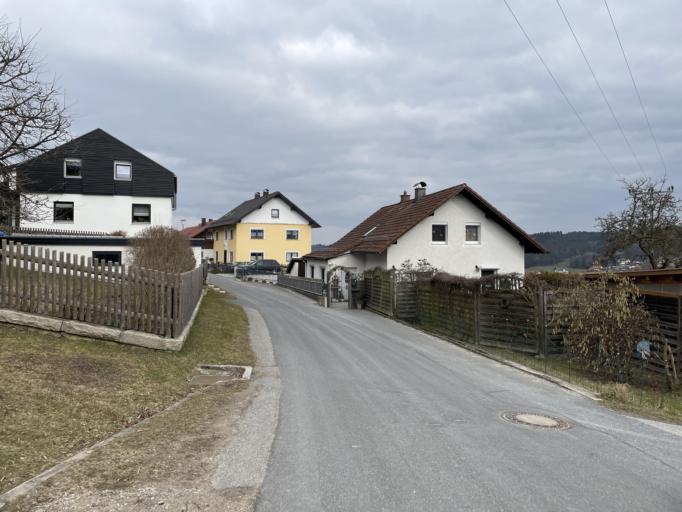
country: DE
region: Bavaria
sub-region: Upper Palatinate
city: Runding
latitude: 49.2174
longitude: 12.7656
